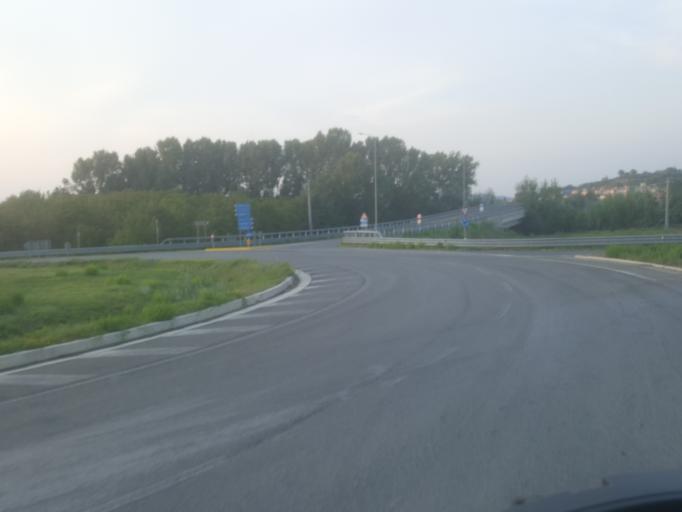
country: IT
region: Tuscany
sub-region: Province of Florence
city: Certaldo
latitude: 43.5336
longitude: 11.0403
